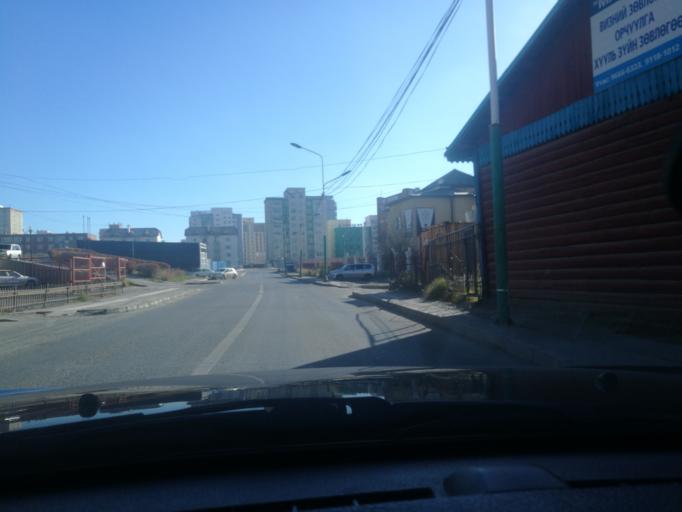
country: MN
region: Ulaanbaatar
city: Ulaanbaatar
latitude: 47.9147
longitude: 106.9275
